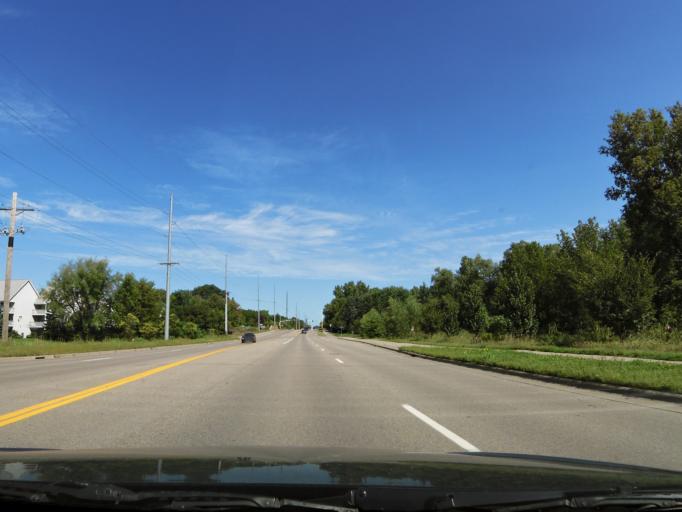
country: US
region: Minnesota
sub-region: Hennepin County
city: Minnetonka
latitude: 44.9210
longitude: -93.5033
